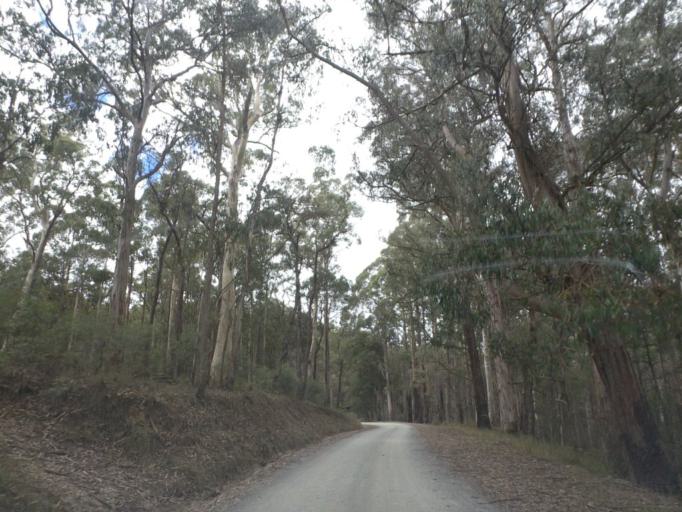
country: AU
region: Victoria
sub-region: Murrindindi
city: Alexandra
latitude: -37.4592
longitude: 145.9712
